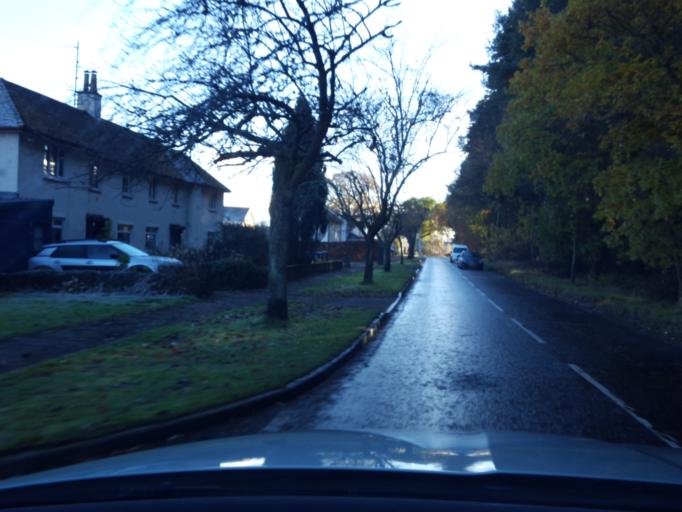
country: GB
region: Scotland
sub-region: Perth and Kinross
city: Scone
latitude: 56.4255
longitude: -3.4154
